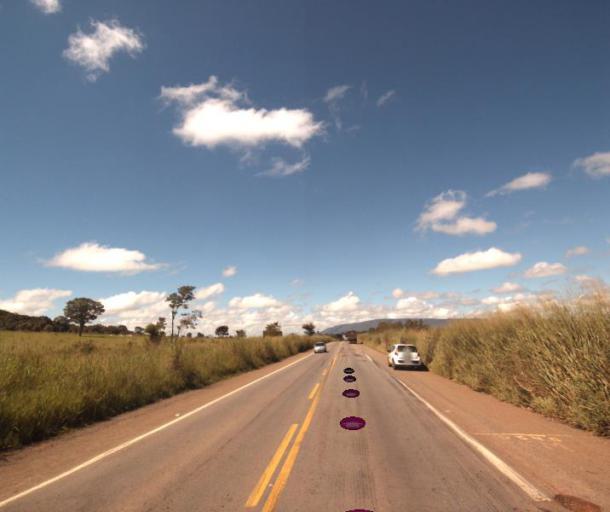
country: BR
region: Goias
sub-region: Jaragua
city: Jaragua
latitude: -15.7078
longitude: -49.3311
